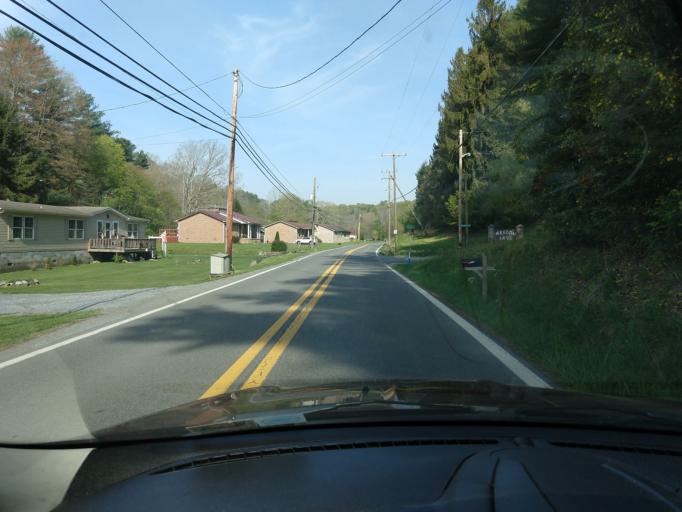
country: US
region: West Virginia
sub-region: Raleigh County
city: Crab Orchard
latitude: 37.7401
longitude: -81.2369
